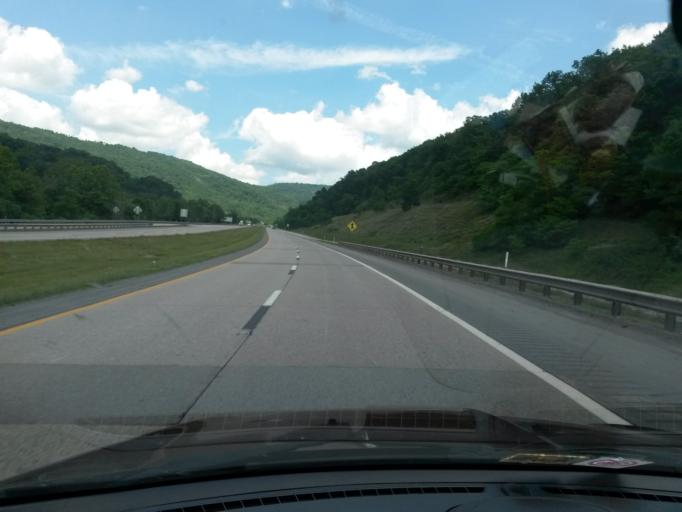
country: US
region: West Virginia
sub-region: Summers County
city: Hinton
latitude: 37.8076
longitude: -80.8154
